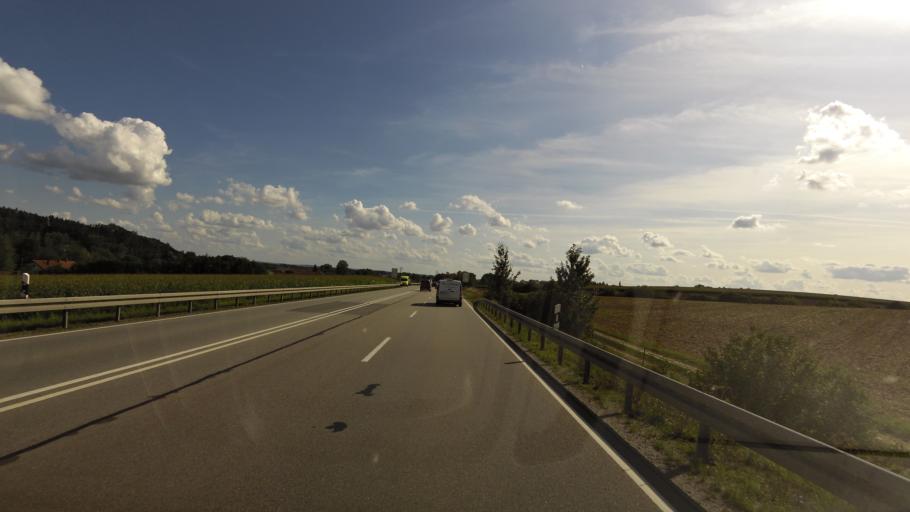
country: DE
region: Bavaria
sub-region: Lower Bavaria
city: Steinach
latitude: 48.9680
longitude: 12.6253
